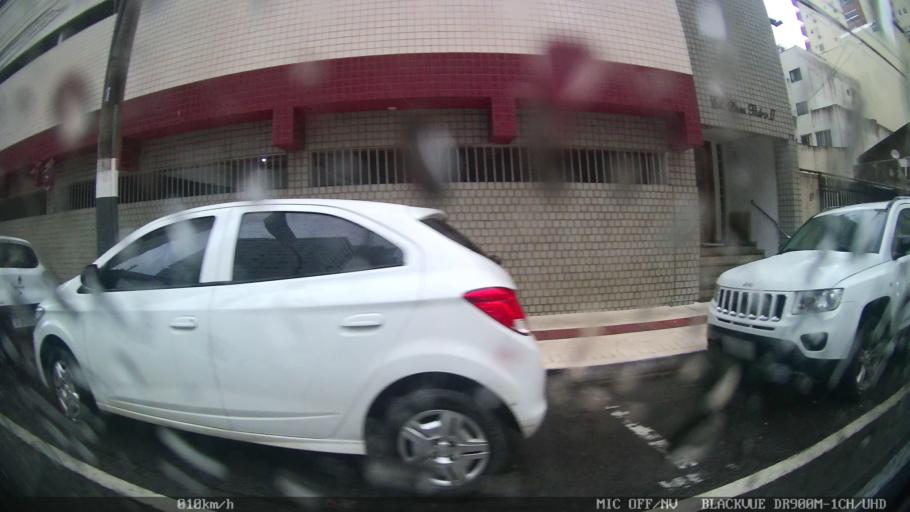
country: BR
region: Santa Catarina
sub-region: Balneario Camboriu
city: Balneario Camboriu
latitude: -26.9891
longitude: -48.6312
